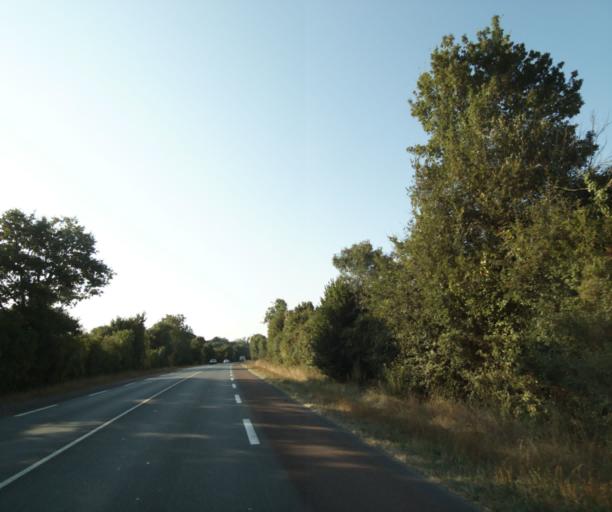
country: FR
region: Poitou-Charentes
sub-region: Departement de la Charente-Maritime
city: Cabariot
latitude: 45.9456
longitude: -0.8653
